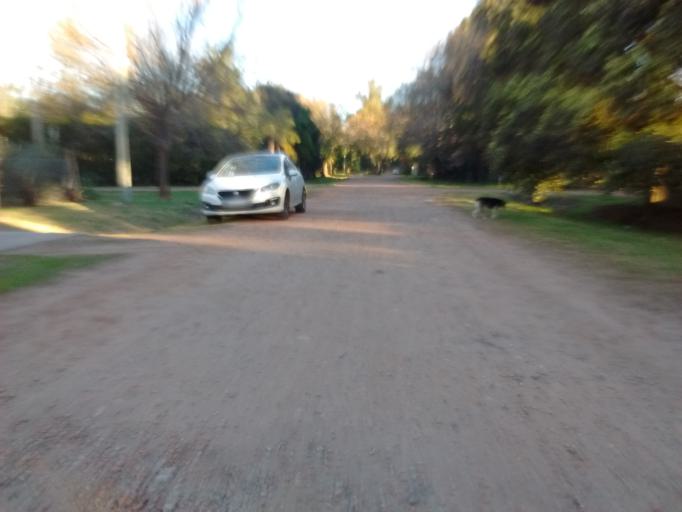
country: AR
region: Santa Fe
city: Funes
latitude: -32.9148
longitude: -60.8329
